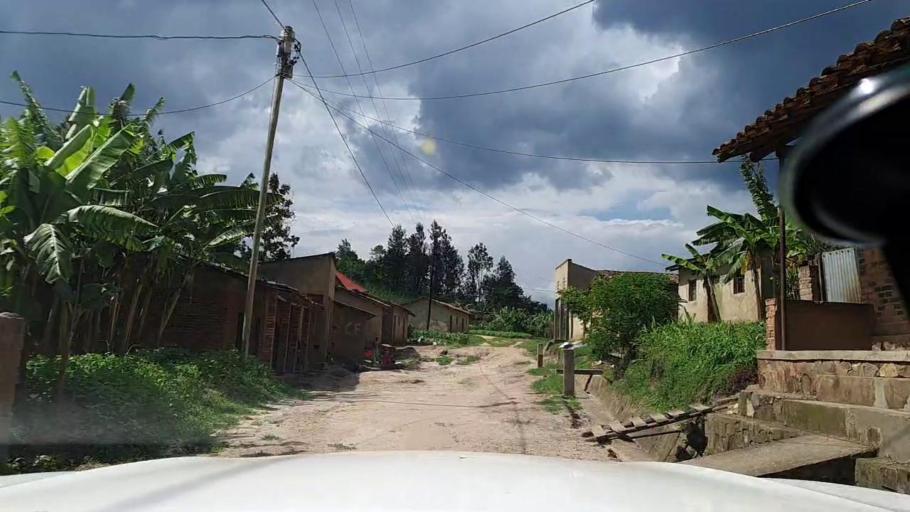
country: RW
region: Southern Province
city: Gitarama
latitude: -1.8323
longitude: 29.8056
